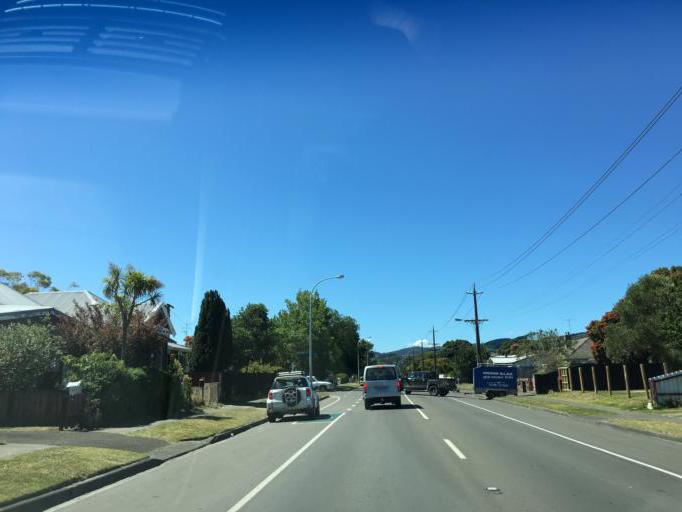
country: NZ
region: Gisborne
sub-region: Gisborne District
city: Gisborne
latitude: -38.6631
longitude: 178.0066
